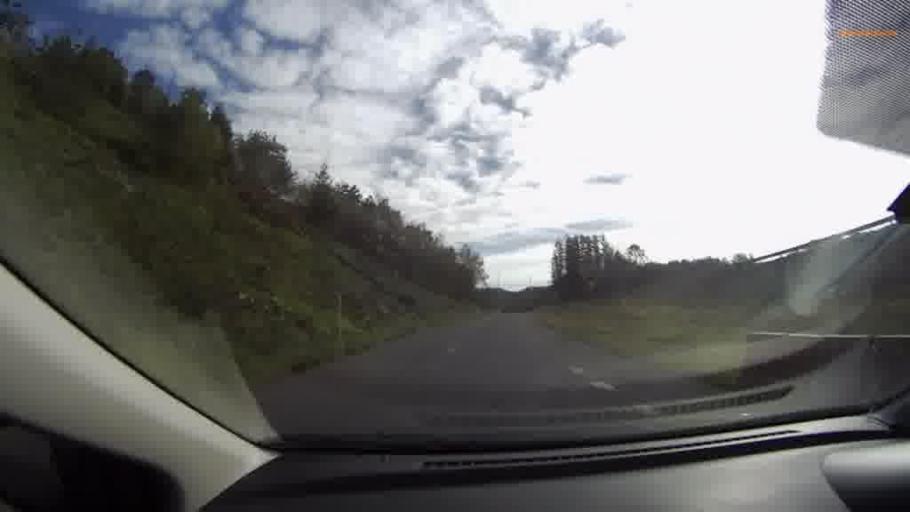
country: JP
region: Hokkaido
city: Kushiro
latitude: 43.0797
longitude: 143.9619
